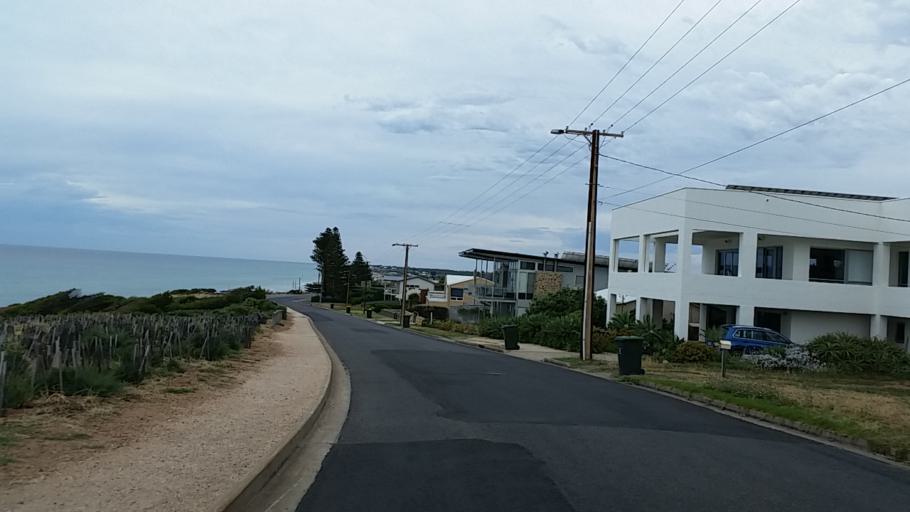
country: AU
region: South Australia
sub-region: Onkaparinga
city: Port Willunga
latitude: -35.3336
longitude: 138.4484
